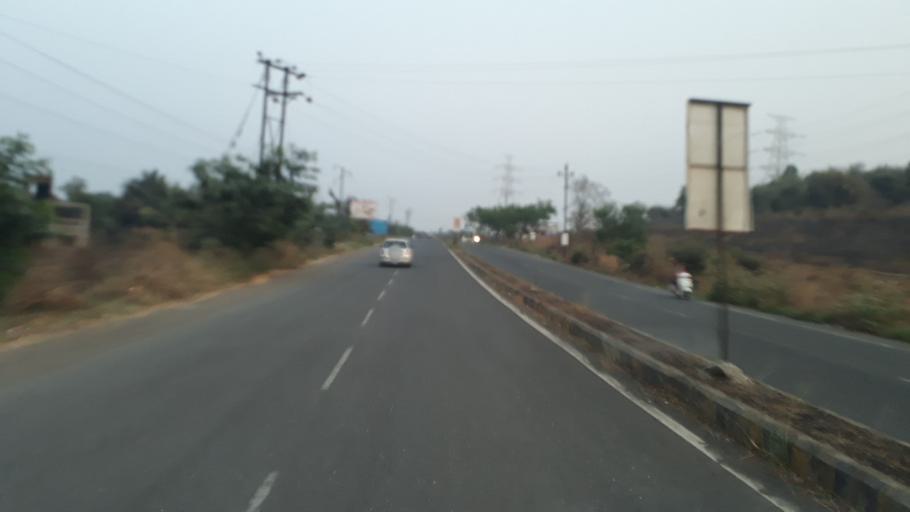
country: IN
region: Maharashtra
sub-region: Raigarh
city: Neral
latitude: 19.0168
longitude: 73.3206
